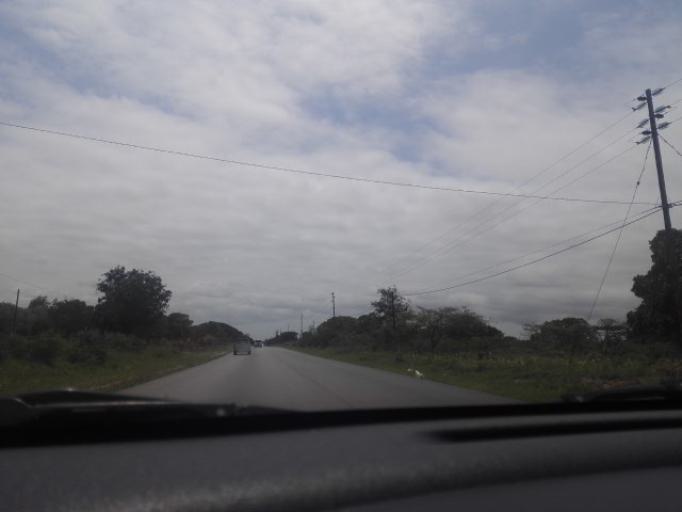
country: MZ
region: Maputo
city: Manhica
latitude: -25.4106
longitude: 32.7515
